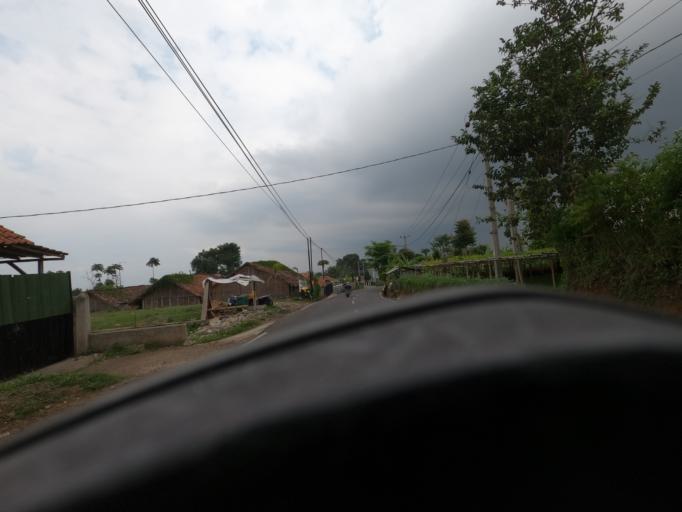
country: ID
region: West Java
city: Cimahi
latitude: -6.8181
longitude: 107.5398
